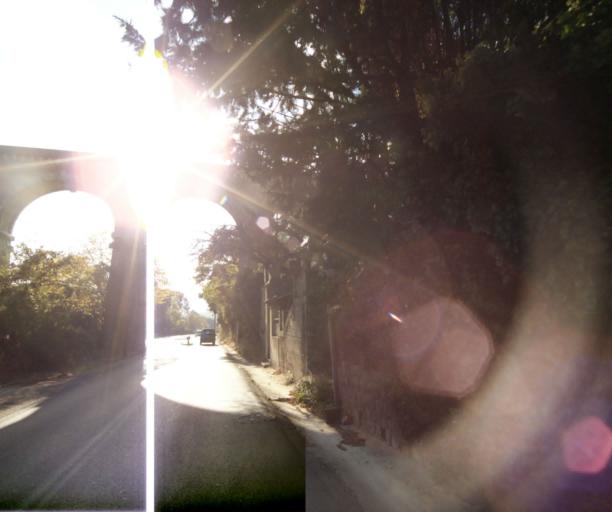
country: FR
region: Provence-Alpes-Cote d'Azur
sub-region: Departement des Bouches-du-Rhone
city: Allauch
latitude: 43.3106
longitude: 5.4999
